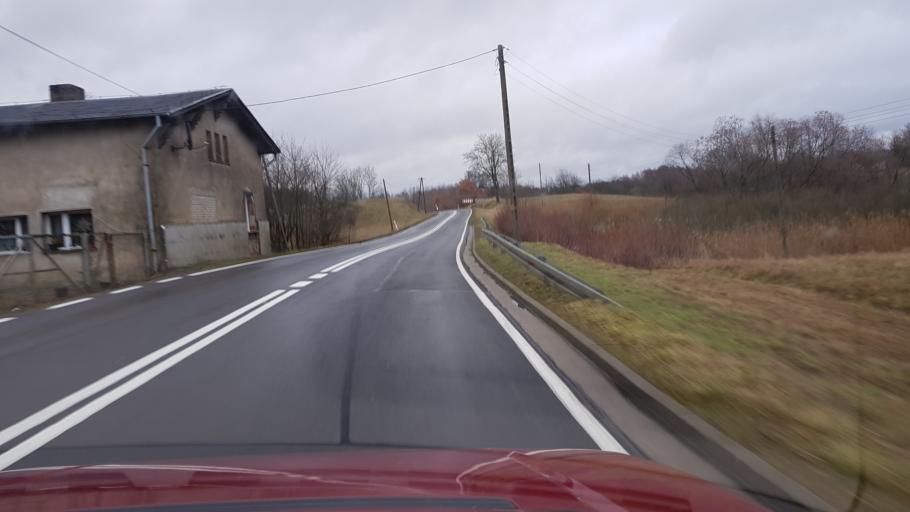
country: PL
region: West Pomeranian Voivodeship
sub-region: Powiat lobeski
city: Wegorzyno
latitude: 53.5222
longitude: 15.6204
